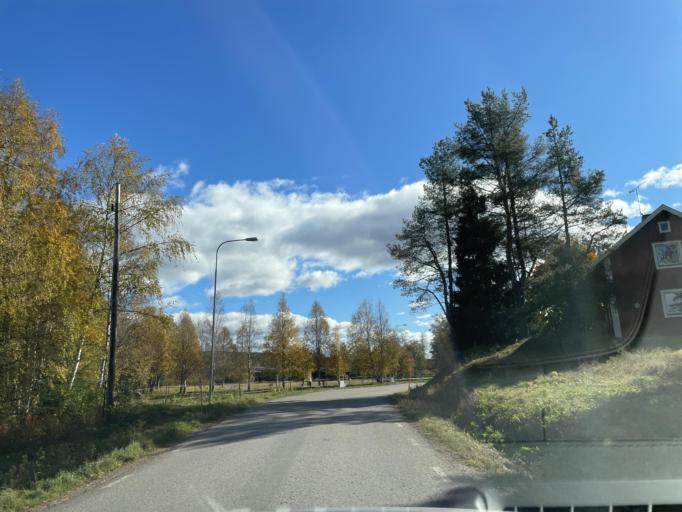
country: SE
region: Dalarna
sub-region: Malung-Saelens kommun
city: Malung
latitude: 61.1609
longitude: 13.2558
